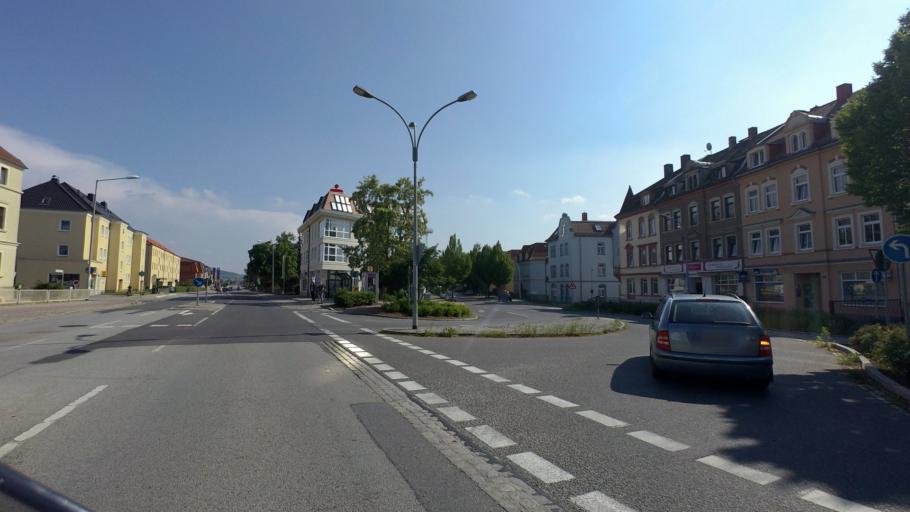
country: DE
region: Saxony
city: Bautzen
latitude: 51.1722
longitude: 14.4239
